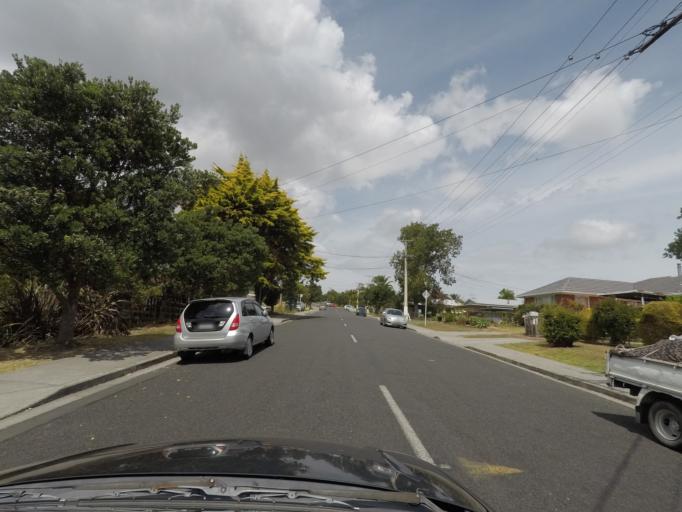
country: NZ
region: Auckland
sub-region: Auckland
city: Waitakere
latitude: -36.8998
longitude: 174.6400
